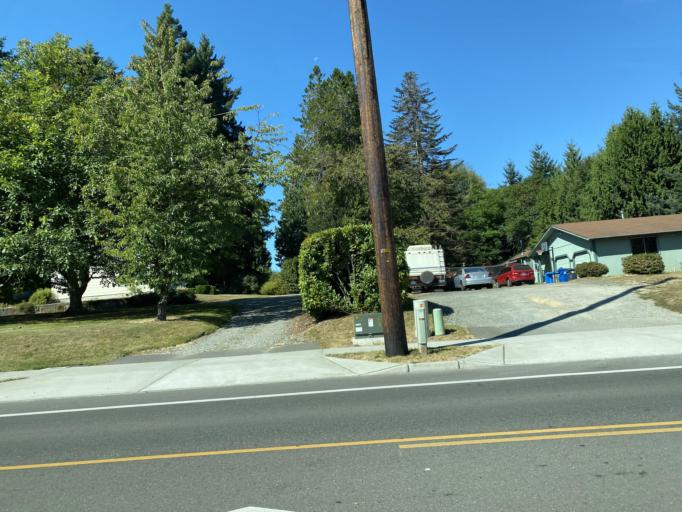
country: US
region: Washington
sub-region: Thurston County
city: Olympia
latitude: 47.0196
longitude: -122.8652
